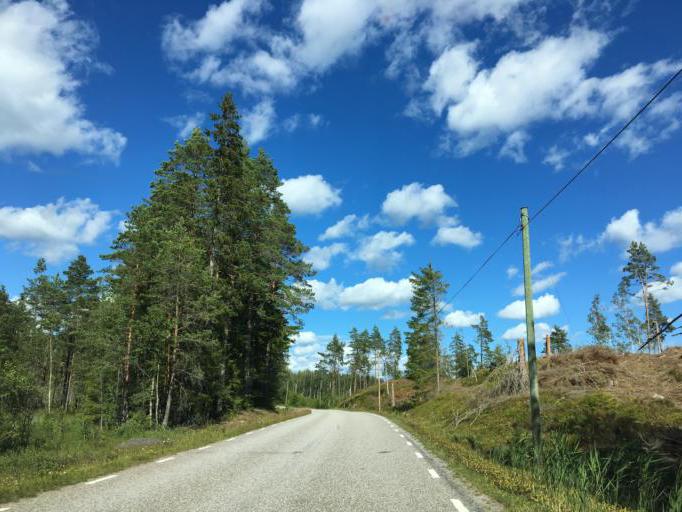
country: SE
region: OErebro
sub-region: Laxa Kommun
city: Laxa
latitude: 58.8114
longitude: 14.6591
